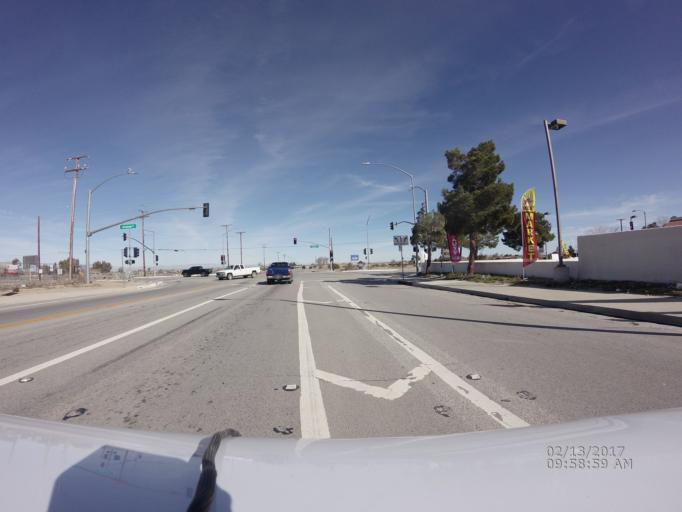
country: US
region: California
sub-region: Los Angeles County
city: Littlerock
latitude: 34.5425
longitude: -117.9748
